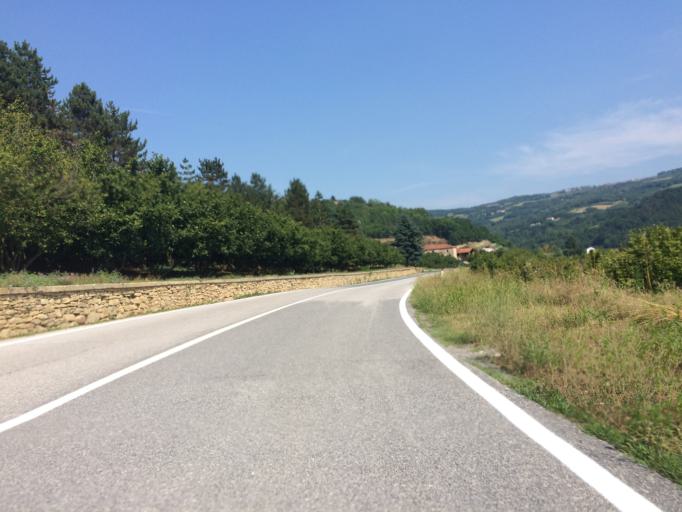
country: IT
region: Piedmont
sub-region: Provincia di Cuneo
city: Torre Bormida
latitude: 44.5615
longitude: 8.1472
